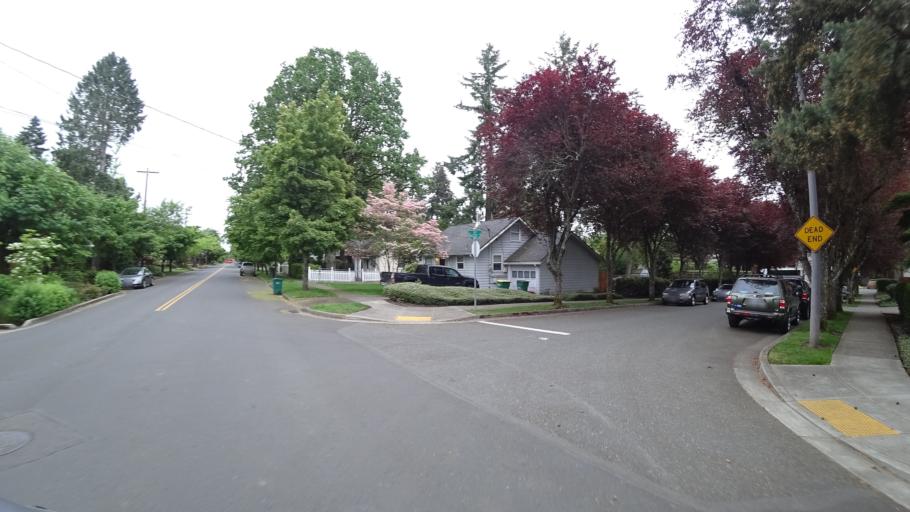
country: US
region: Oregon
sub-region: Washington County
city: Beaverton
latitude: 45.4808
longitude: -122.8085
